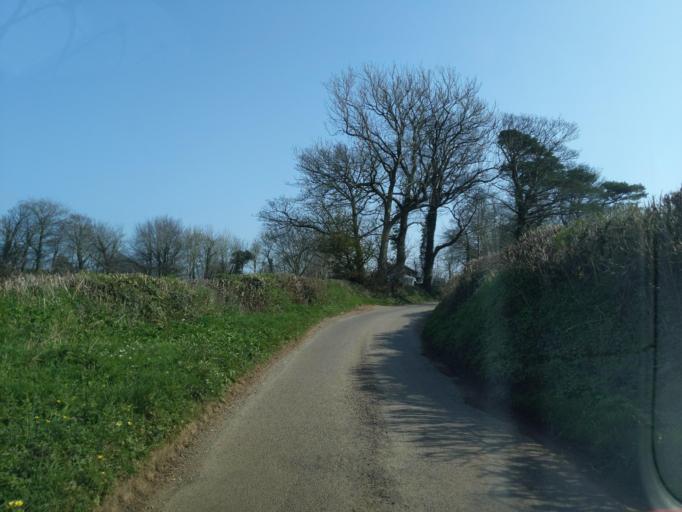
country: GB
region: England
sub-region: Devon
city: Totnes
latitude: 50.4250
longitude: -3.7026
